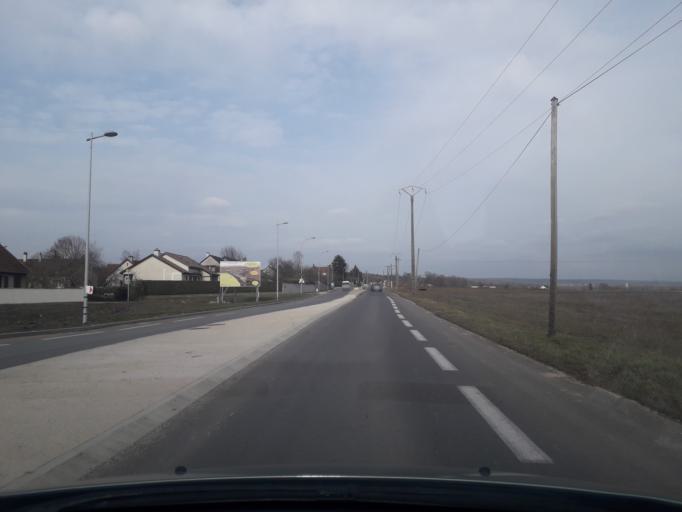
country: FR
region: Bourgogne
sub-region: Departement de la Cote-d'Or
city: Ahuy
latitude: 47.3629
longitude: 5.0298
